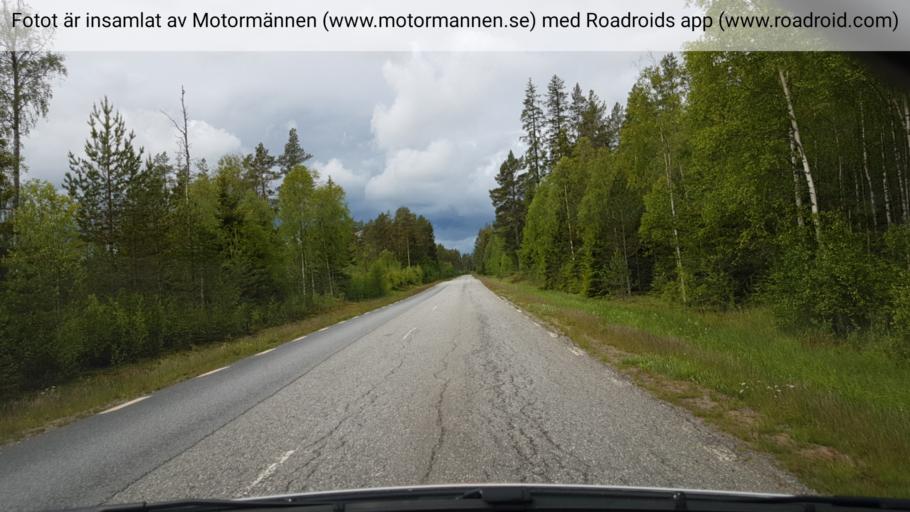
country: SE
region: Vaesterbotten
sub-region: Umea Kommun
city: Hoernefors
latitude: 63.5613
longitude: 19.7224
